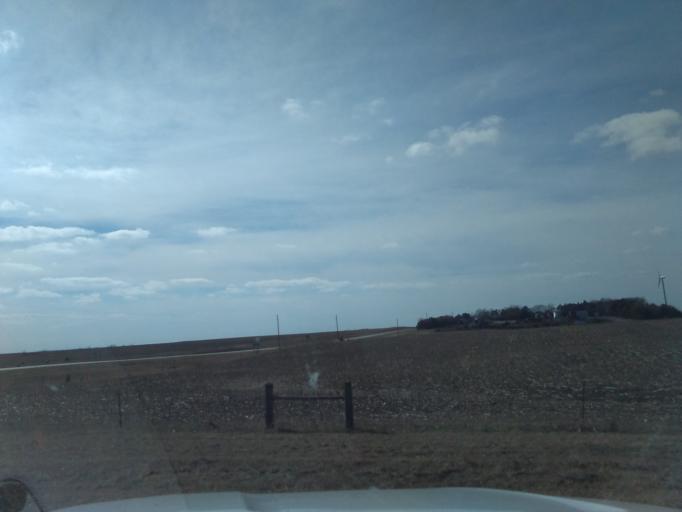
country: US
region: Kansas
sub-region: Washington County
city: Washington
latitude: 40.0455
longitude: -96.9350
